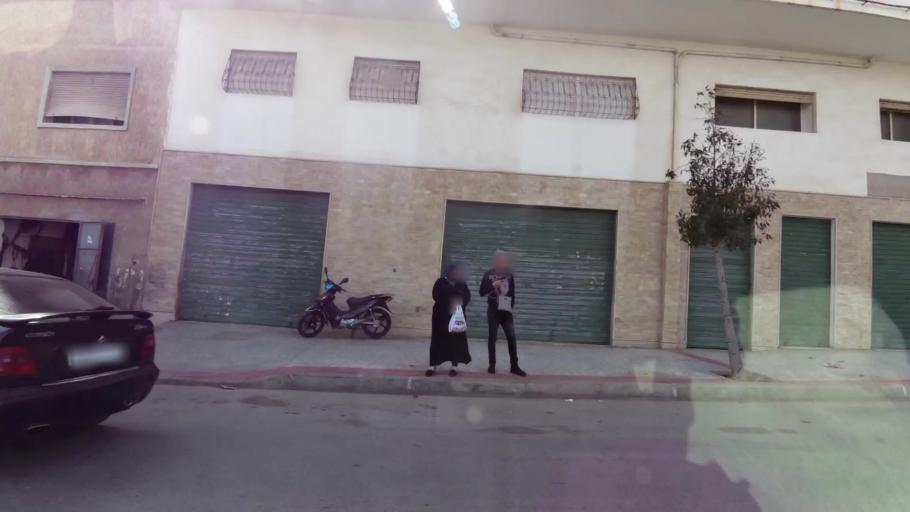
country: MA
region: Tanger-Tetouan
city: Tetouan
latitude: 35.5863
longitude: -5.3564
